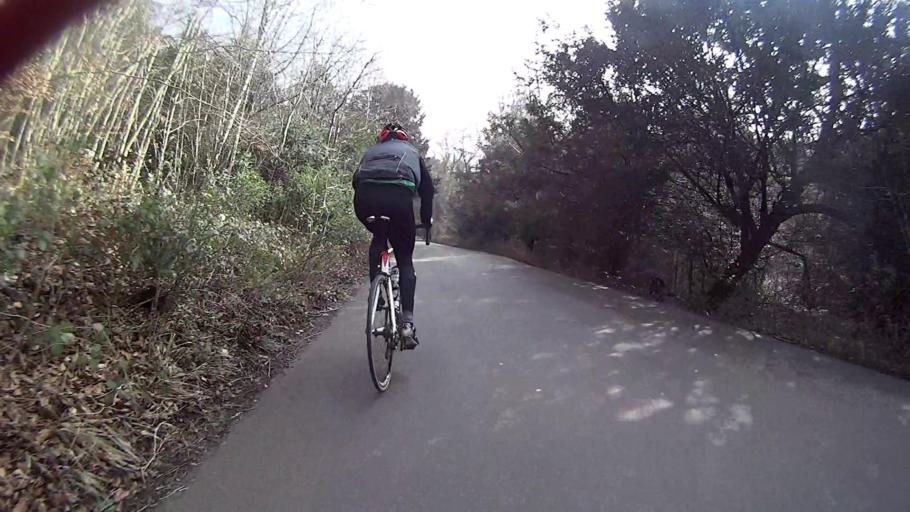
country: GB
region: England
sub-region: Surrey
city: Mickleham
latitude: 51.2514
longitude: -0.3106
